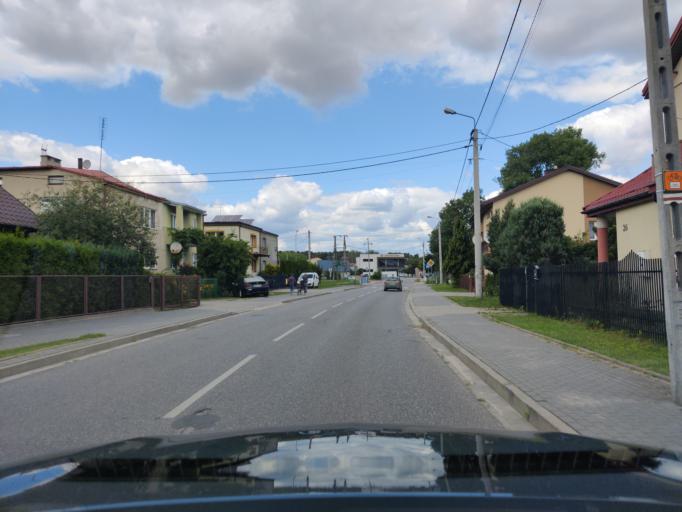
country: PL
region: Masovian Voivodeship
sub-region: Powiat wegrowski
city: Wegrow
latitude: 52.4018
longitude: 22.0201
